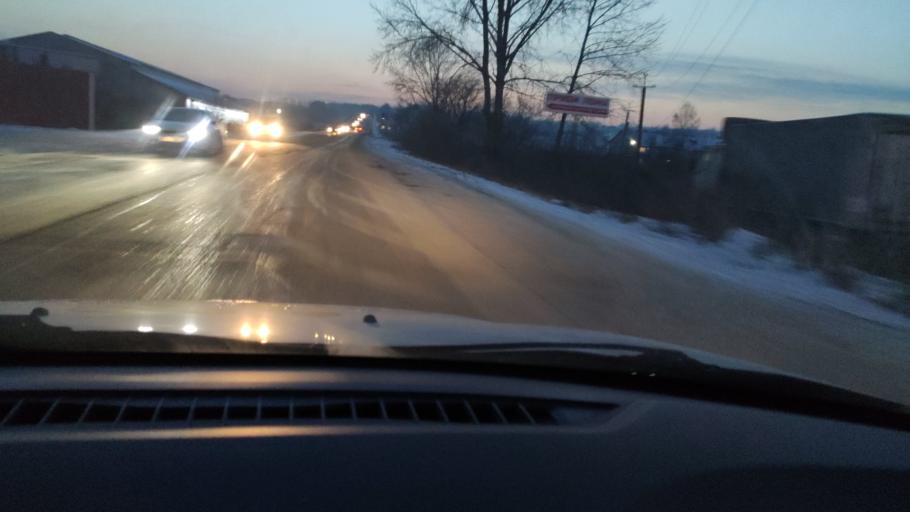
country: RU
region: Perm
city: Kungur
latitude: 57.4253
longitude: 56.9313
